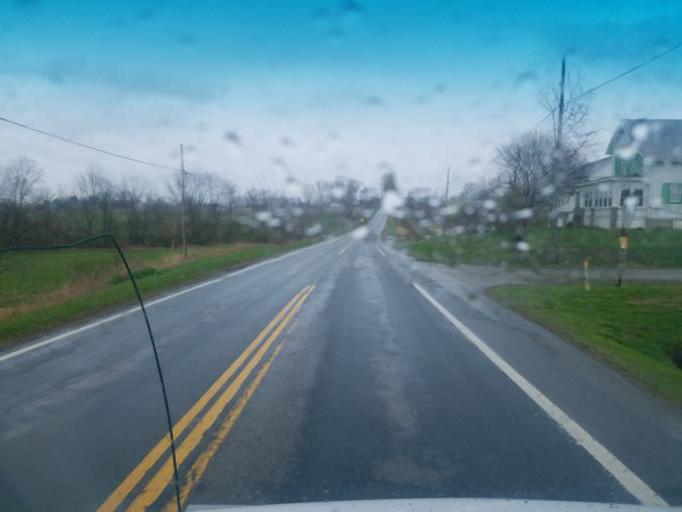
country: US
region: Ohio
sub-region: Wayne County
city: Wooster
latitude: 40.7568
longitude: -81.9308
